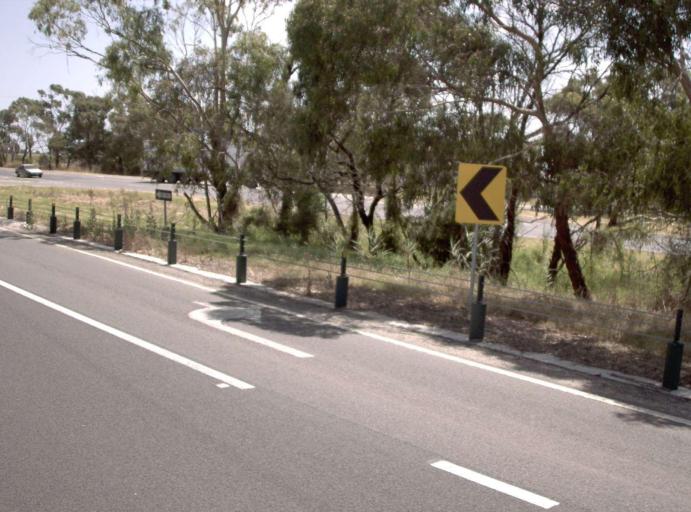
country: AU
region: Victoria
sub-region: Casey
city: Tooradin
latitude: -38.2140
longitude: 145.4153
